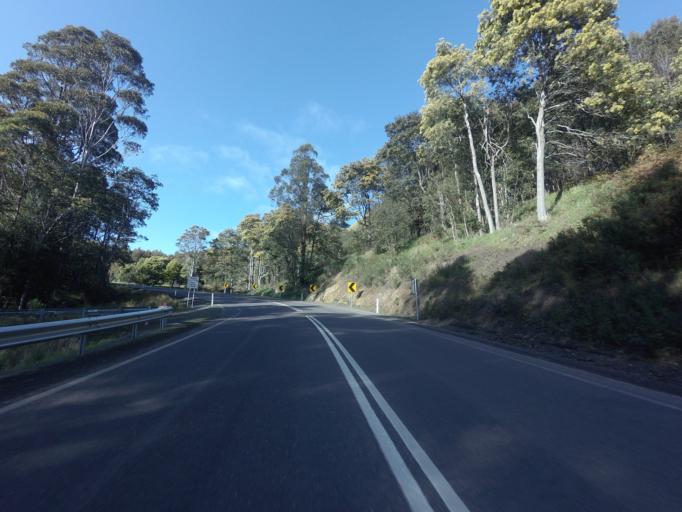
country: AU
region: Tasmania
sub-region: Huon Valley
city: Geeveston
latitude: -43.2520
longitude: 146.9946
